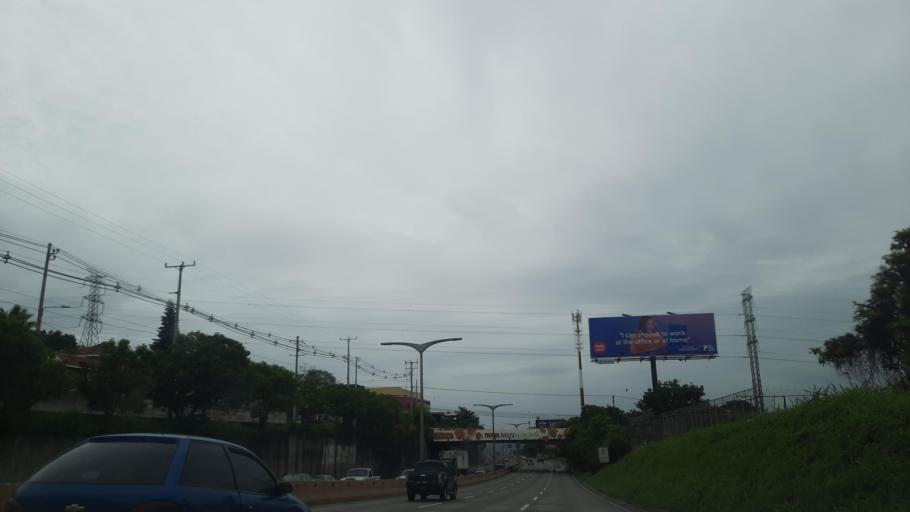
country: SV
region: La Libertad
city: Santa Tecla
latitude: 13.6845
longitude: -89.2778
